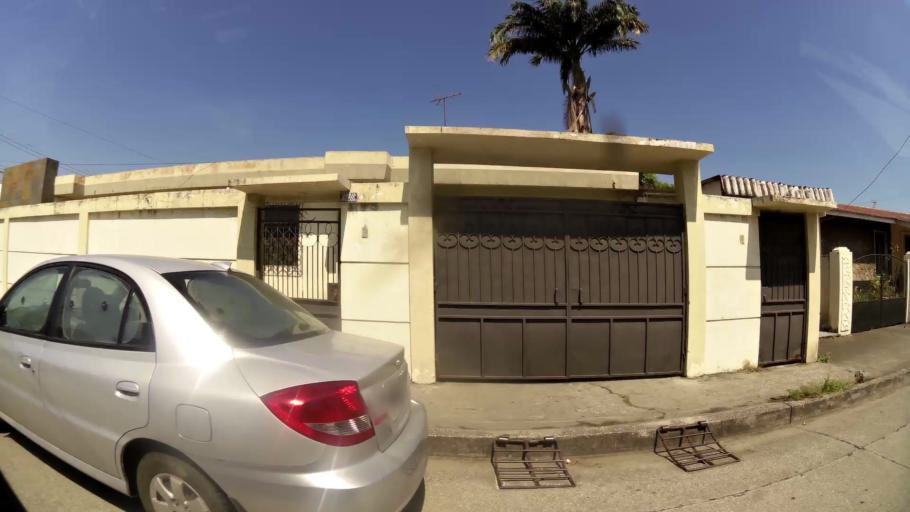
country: EC
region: Guayas
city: Guayaquil
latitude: -2.1672
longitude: -79.9088
